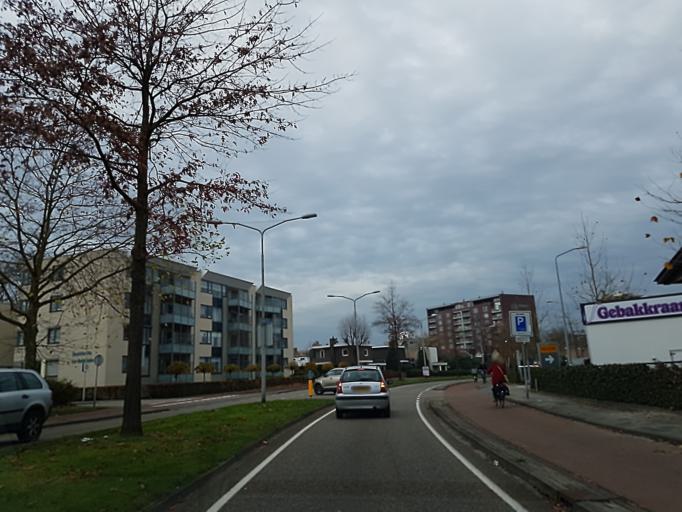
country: NL
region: North Brabant
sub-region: Roosendaal
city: Roosendaal
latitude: 51.5278
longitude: 4.4579
